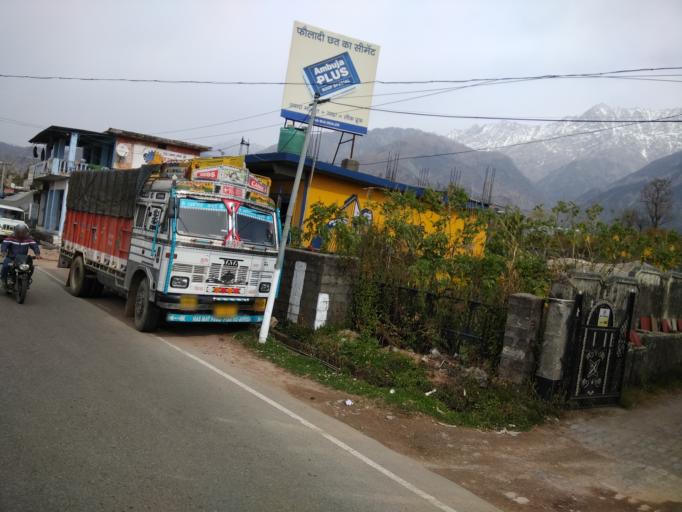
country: IN
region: Himachal Pradesh
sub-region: Kangra
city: Dharmsala
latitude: 32.1921
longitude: 76.3494
